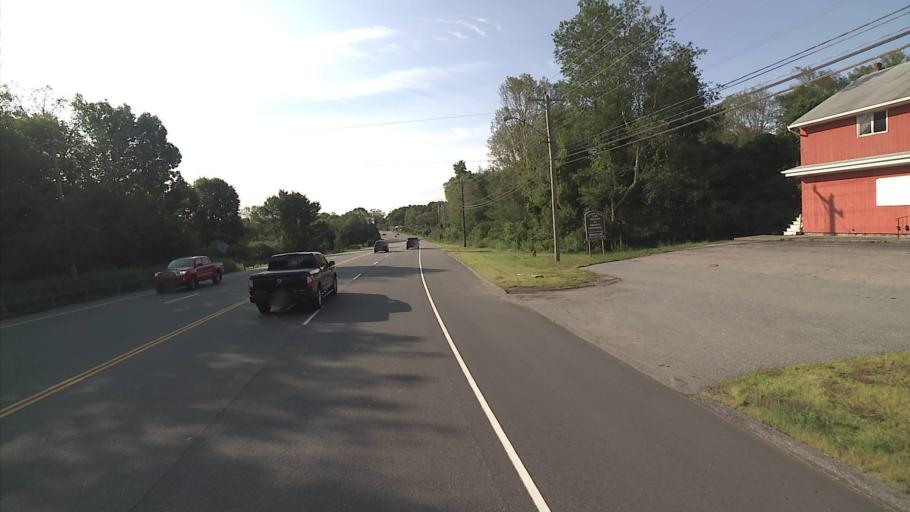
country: US
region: Connecticut
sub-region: New London County
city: Pawcatuck
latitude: 41.4092
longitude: -71.8537
